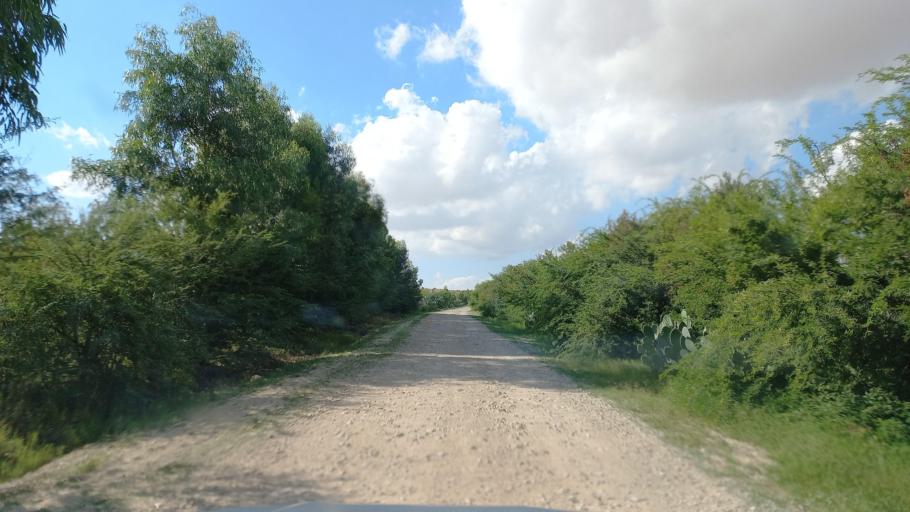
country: TN
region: Al Qasrayn
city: Sbiba
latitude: 35.3364
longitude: 9.0806
